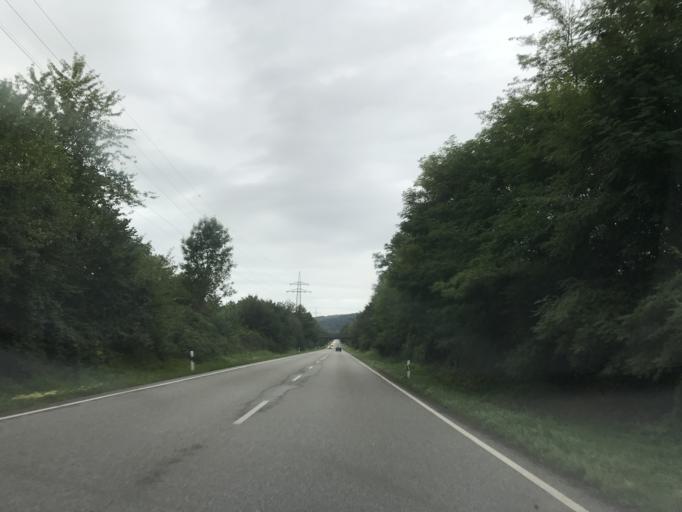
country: CH
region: Aargau
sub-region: Bezirk Rheinfelden
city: Mumpf
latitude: 47.5661
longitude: 7.9224
